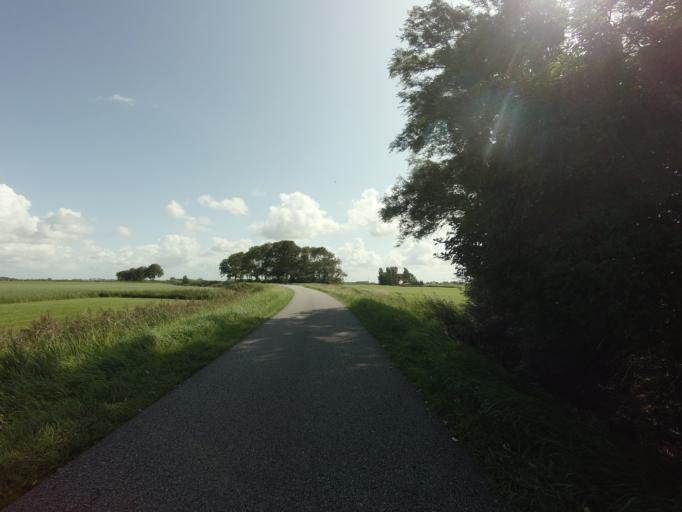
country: NL
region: Friesland
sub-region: Sudwest Fryslan
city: Makkum
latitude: 53.0646
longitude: 5.4476
